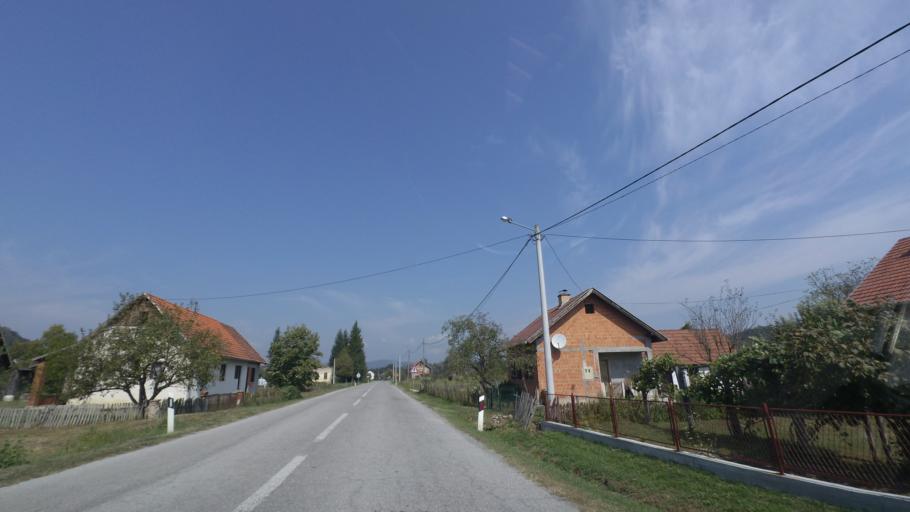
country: HR
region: Sisacko-Moslavacka
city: Dvor
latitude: 45.0940
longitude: 16.2970
